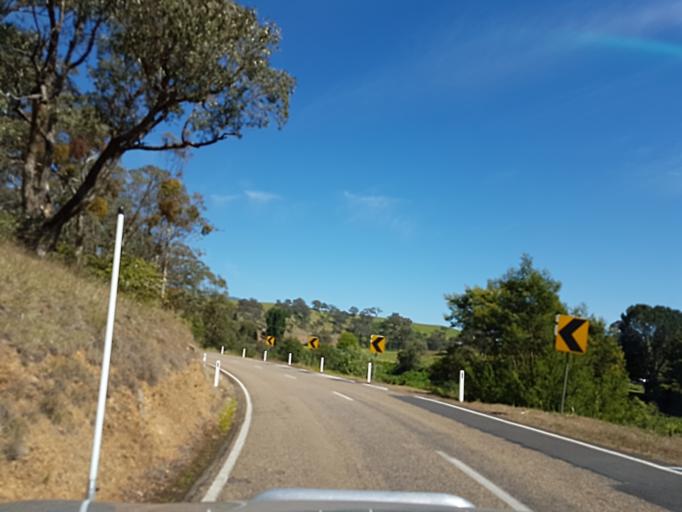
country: AU
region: Victoria
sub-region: East Gippsland
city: Bairnsdale
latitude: -37.3913
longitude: 147.8361
